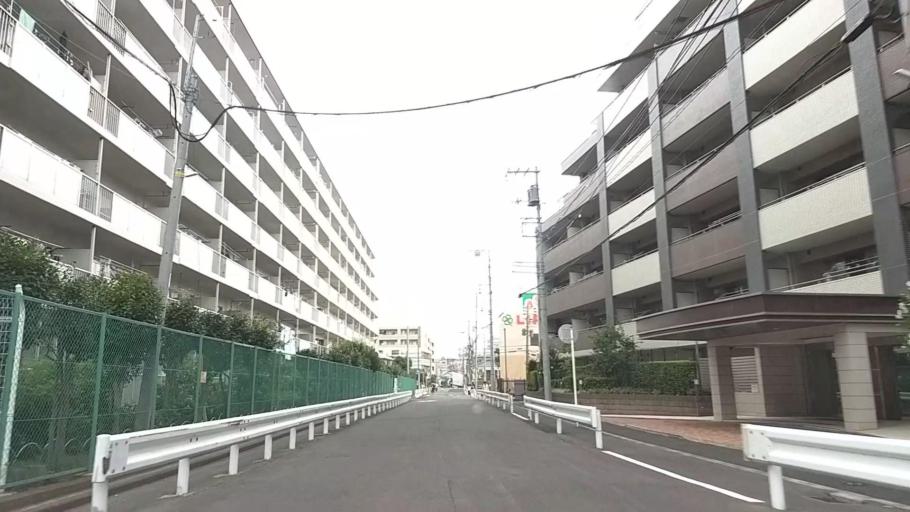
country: JP
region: Kanagawa
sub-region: Kawasaki-shi
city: Kawasaki
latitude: 35.4997
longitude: 139.6787
